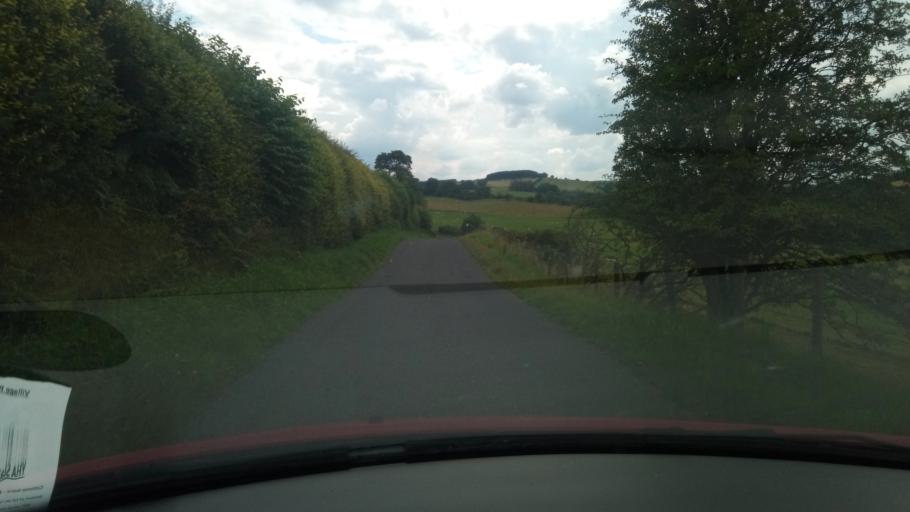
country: GB
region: Scotland
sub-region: The Scottish Borders
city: Jedburgh
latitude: 55.4052
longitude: -2.6471
